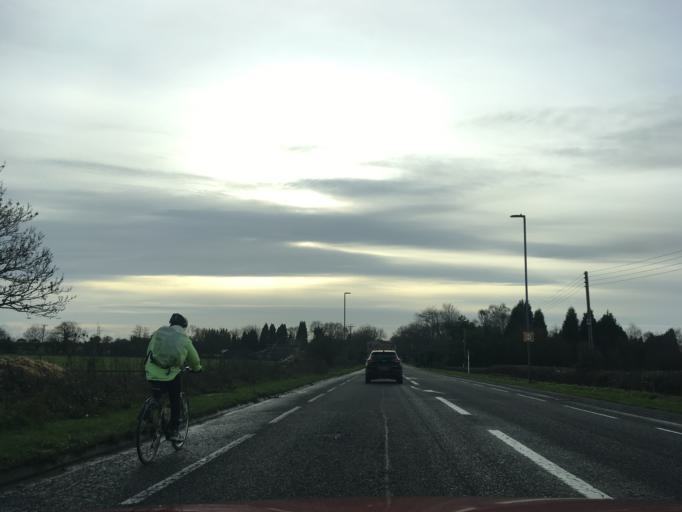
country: GB
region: England
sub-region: South Gloucestershire
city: Alveston
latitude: 51.5710
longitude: -2.5486
